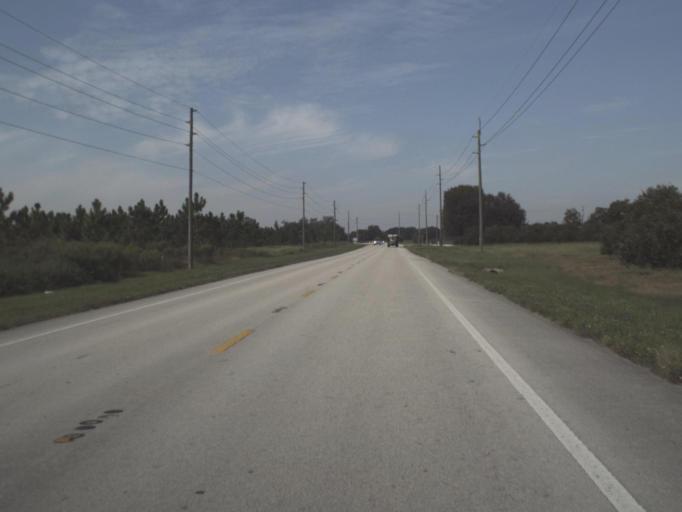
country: US
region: Florida
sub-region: Highlands County
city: Avon Park
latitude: 27.5619
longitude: -81.6549
